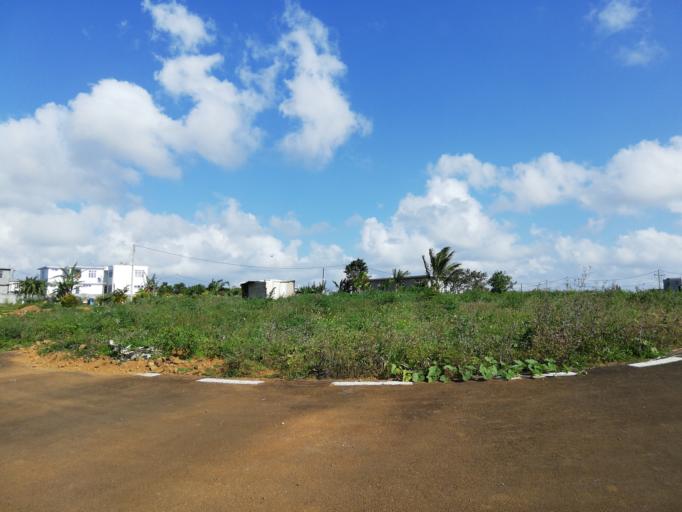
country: MU
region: Moka
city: Verdun
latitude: -20.2248
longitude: 57.5479
